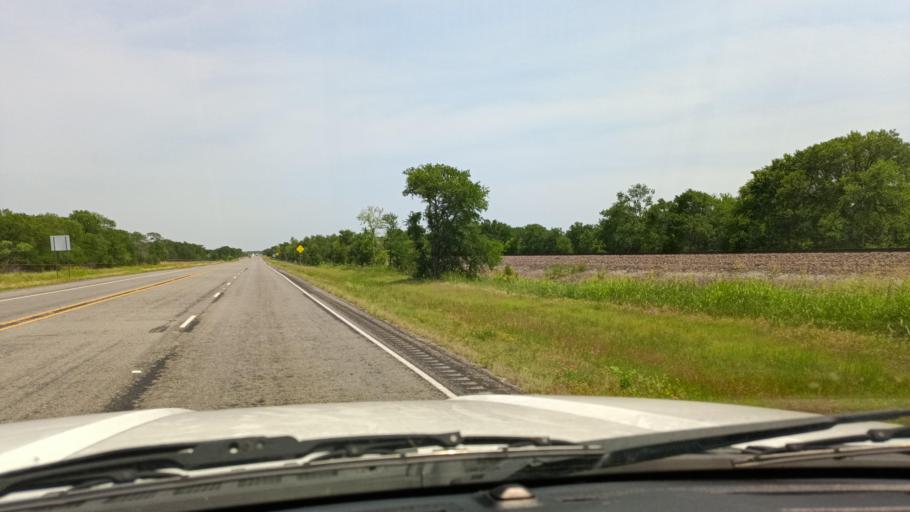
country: US
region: Texas
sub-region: Bell County
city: Rogers
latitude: 30.8973
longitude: -97.1683
